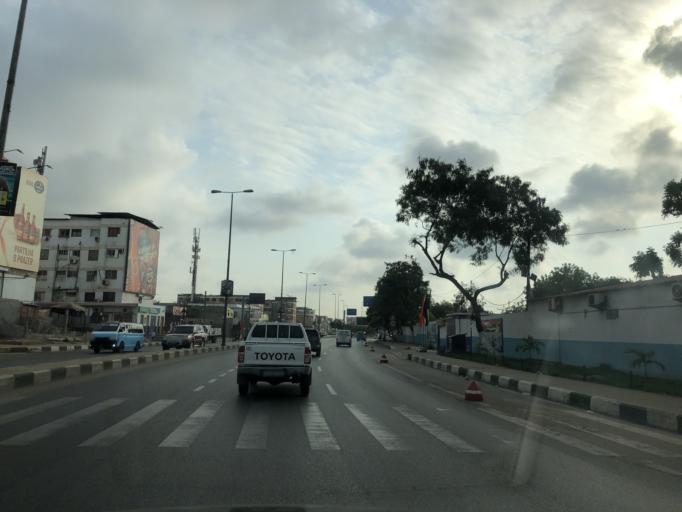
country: AO
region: Luanda
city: Luanda
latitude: -8.8489
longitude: 13.2265
